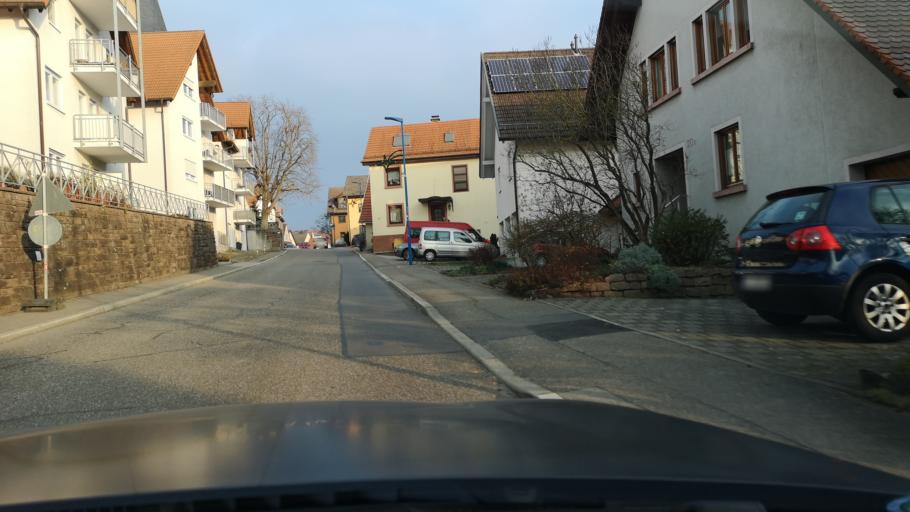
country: DE
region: Baden-Wuerttemberg
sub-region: Karlsruhe Region
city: Ettlingen
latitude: 48.9311
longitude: 8.4600
